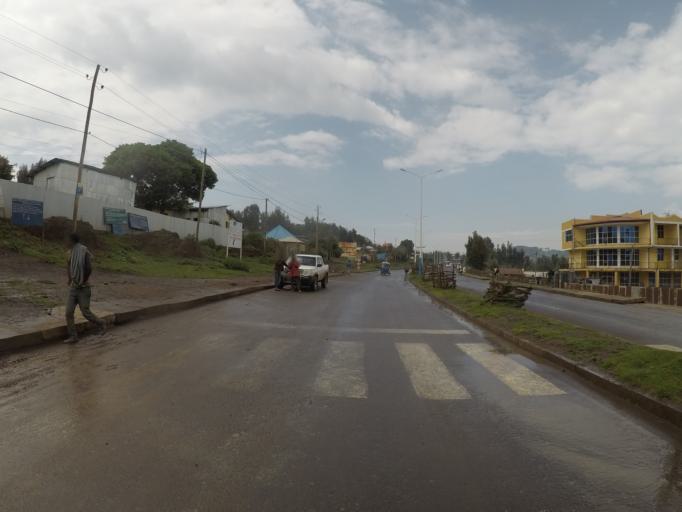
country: ET
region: Amhara
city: Debark'
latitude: 13.1472
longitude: 37.8944
